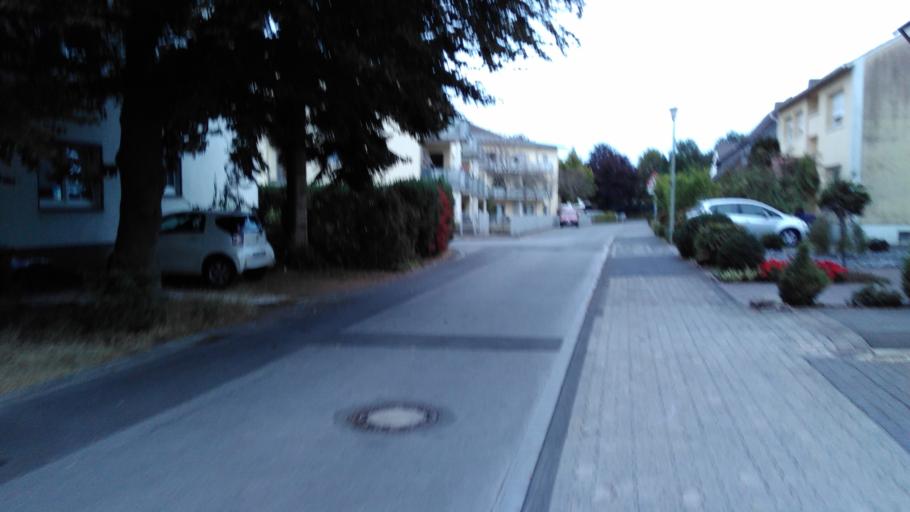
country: DE
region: North Rhine-Westphalia
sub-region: Regierungsbezirk Detmold
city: Verl
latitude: 51.8819
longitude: 8.5027
